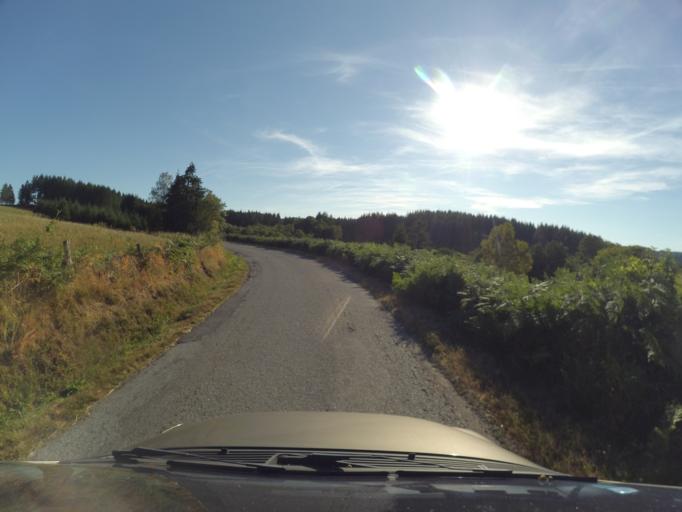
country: FR
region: Limousin
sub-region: Departement de la Creuse
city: Banize
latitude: 45.7573
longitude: 2.0306
